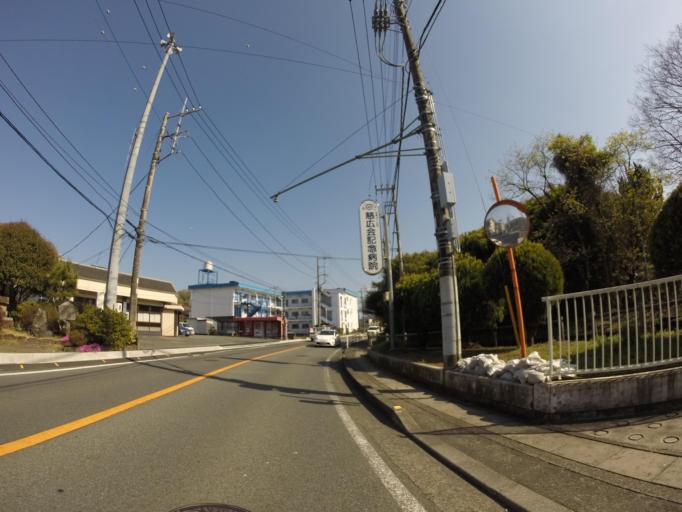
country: JP
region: Shizuoka
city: Mishima
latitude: 35.0389
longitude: 138.9255
